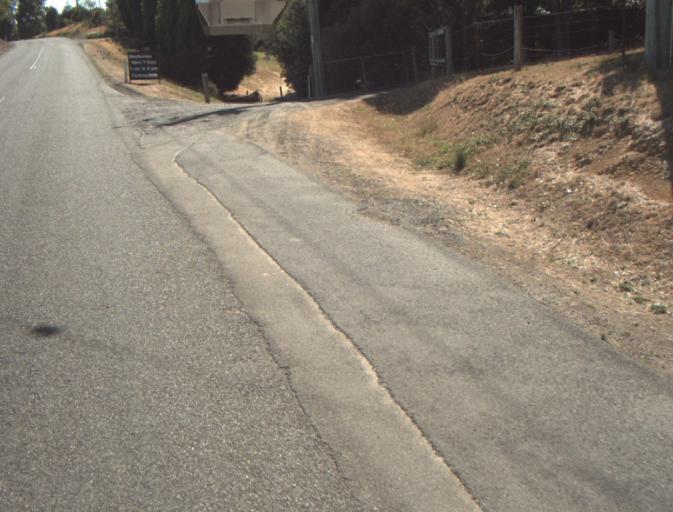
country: AU
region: Tasmania
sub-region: Launceston
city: Mayfield
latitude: -41.2095
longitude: 147.2141
